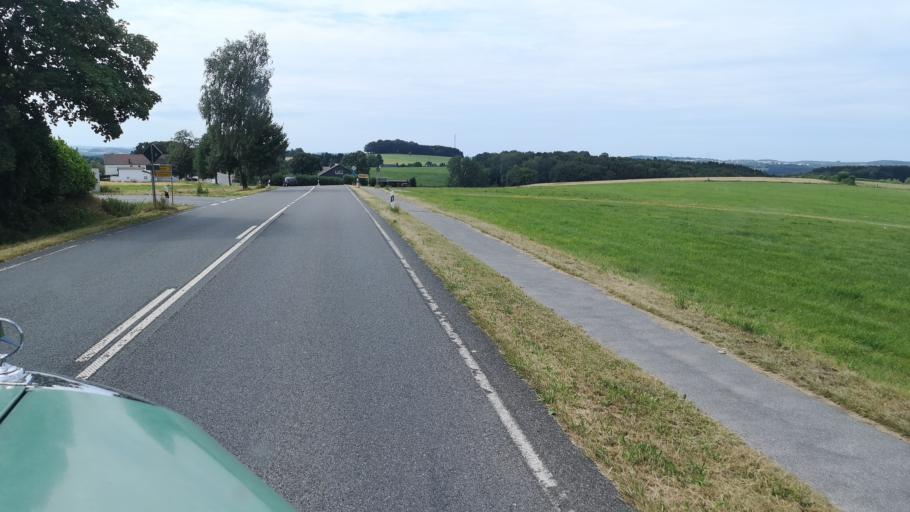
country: DE
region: North Rhine-Westphalia
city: Radevormwald
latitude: 51.1814
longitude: 7.3636
